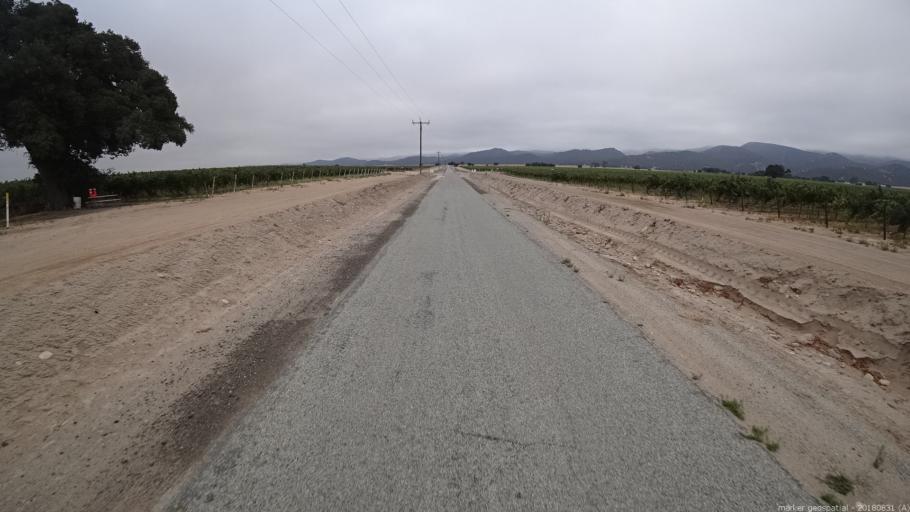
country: US
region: California
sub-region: Monterey County
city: King City
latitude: 36.1161
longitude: -121.0874
